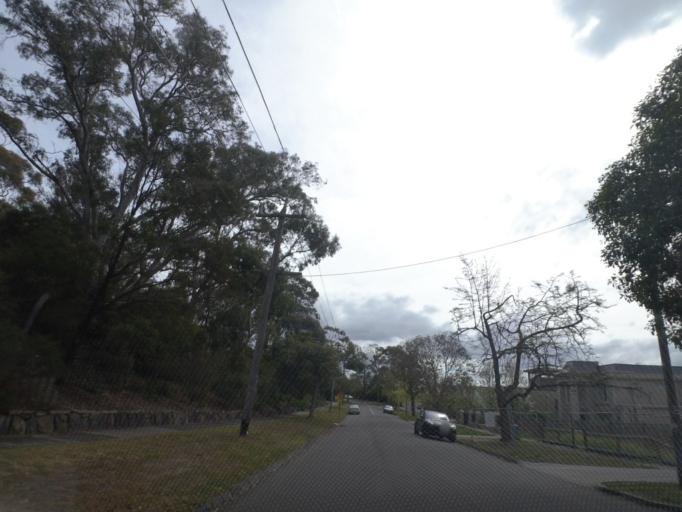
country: AU
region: Victoria
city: Mont Albert
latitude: -37.8094
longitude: 145.0906
